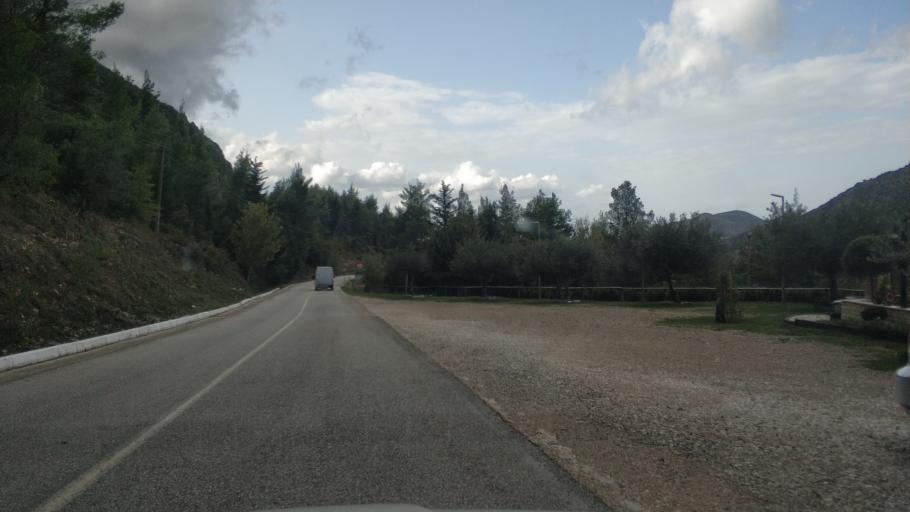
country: AL
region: Vlore
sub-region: Rrethi i Vlores
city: Orikum
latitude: 40.2566
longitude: 19.5294
